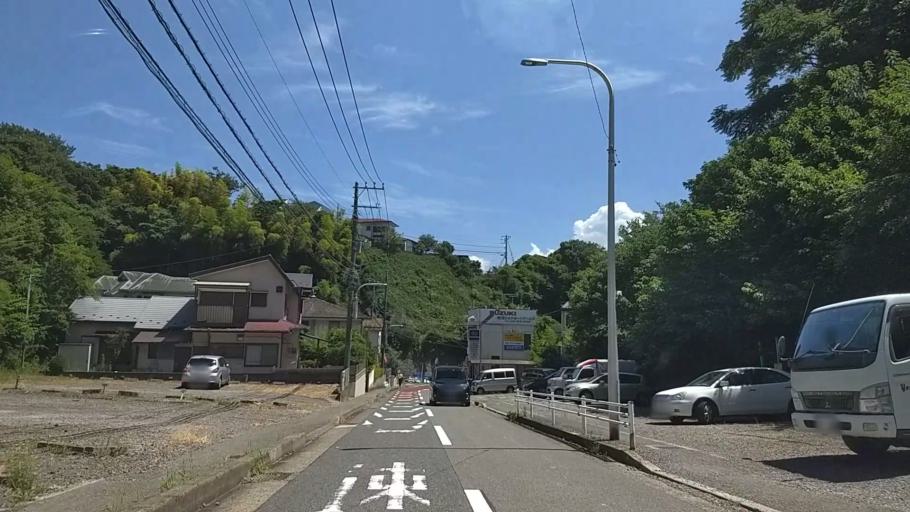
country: JP
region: Kanagawa
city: Zushi
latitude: 35.3018
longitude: 139.6006
